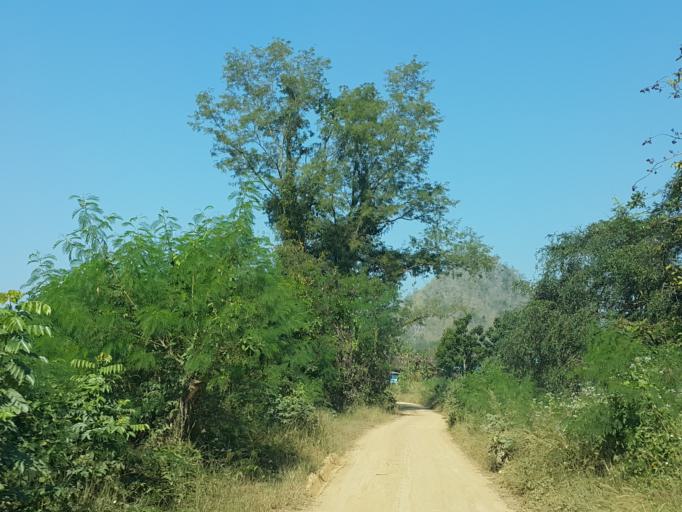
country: TH
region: Sukhothai
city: Thung Saliam
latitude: 17.3419
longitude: 99.4433
